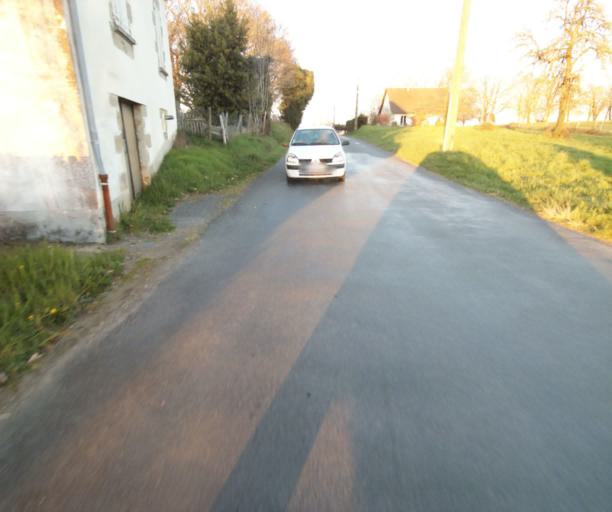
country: FR
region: Limousin
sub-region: Departement de la Correze
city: Sainte-Fereole
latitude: 45.2916
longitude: 1.5681
